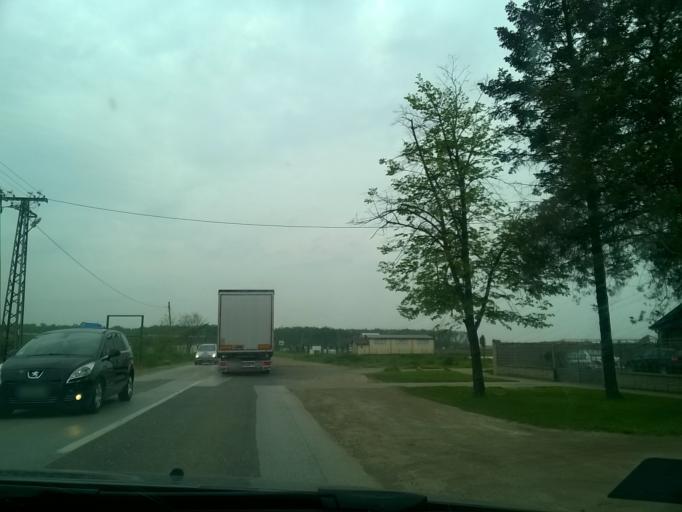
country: RS
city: Jarak
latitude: 44.9086
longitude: 19.7647
